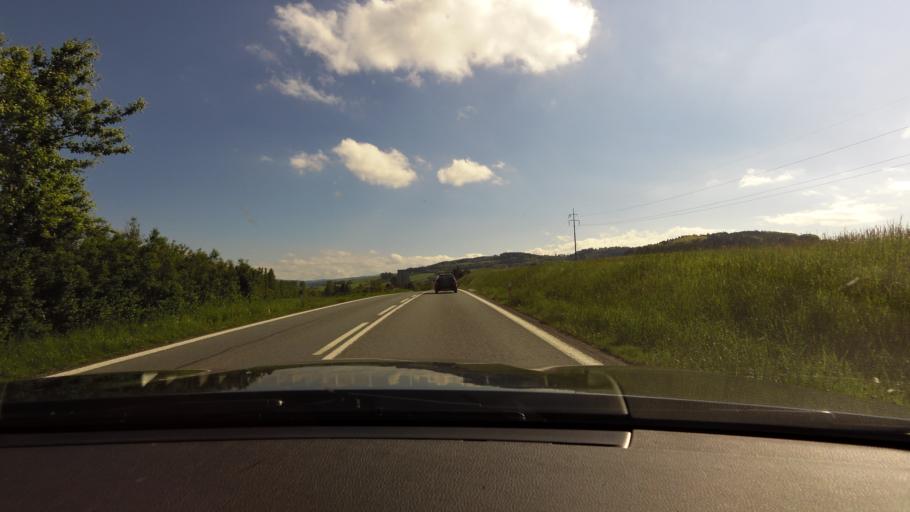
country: CZ
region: Plzensky
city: Klatovy
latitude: 49.3616
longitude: 13.2993
